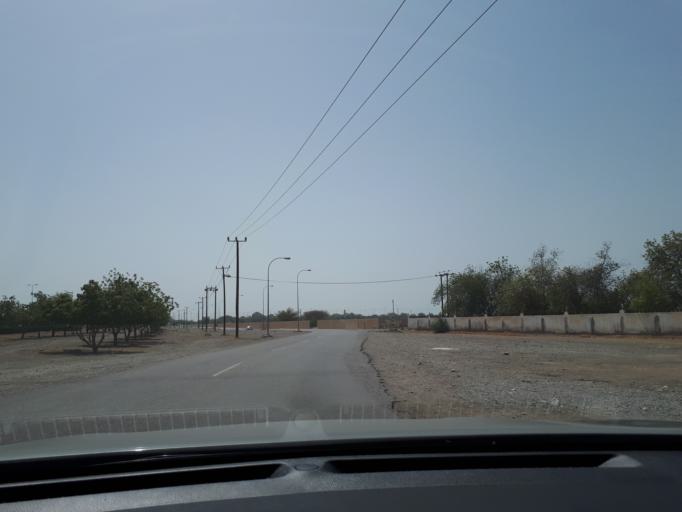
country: OM
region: Muhafazat Masqat
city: As Sib al Jadidah
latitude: 23.6936
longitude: 58.0582
